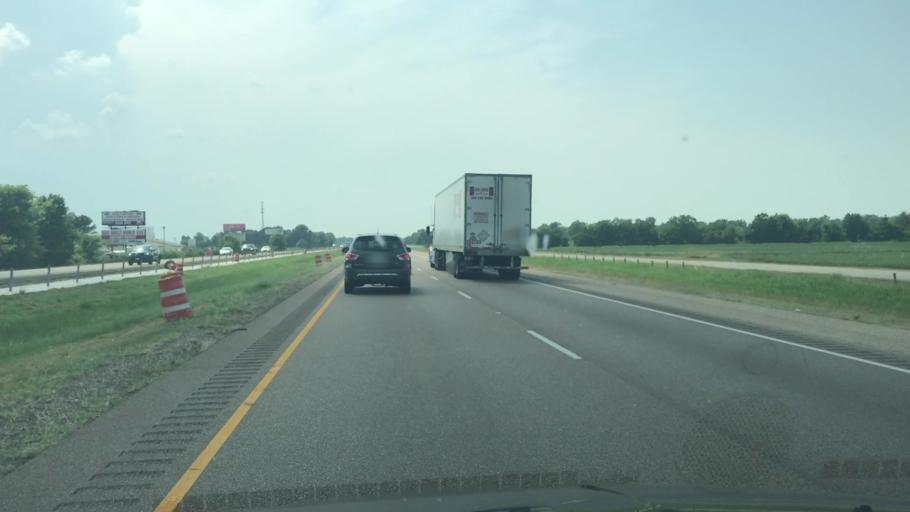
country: US
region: Arkansas
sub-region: Crittenden County
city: West Memphis
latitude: 35.1491
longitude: -90.3471
